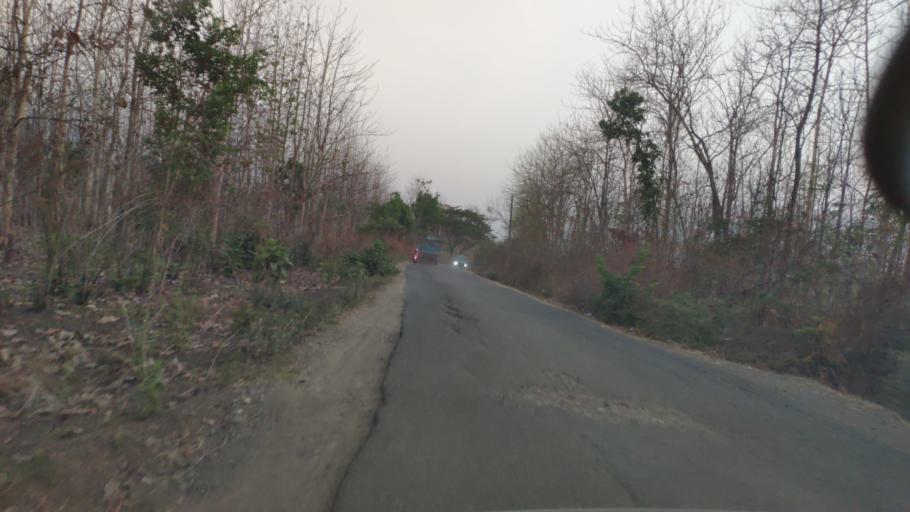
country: ID
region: Central Java
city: Ngliron
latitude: -7.1316
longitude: 111.4233
